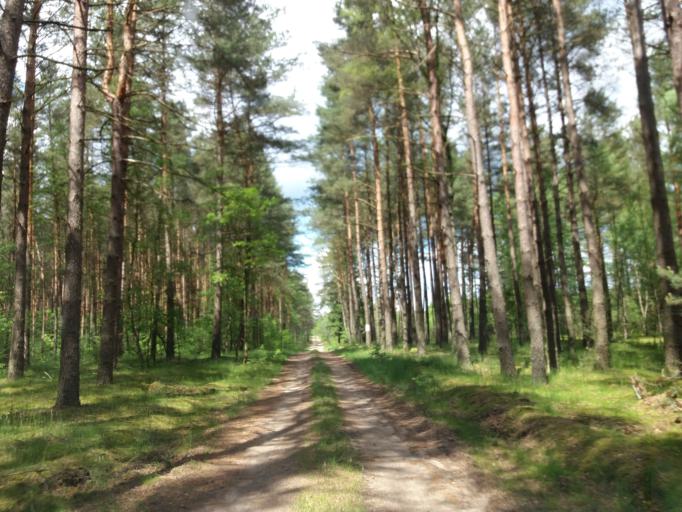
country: PL
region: West Pomeranian Voivodeship
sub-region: Powiat choszczenski
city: Drawno
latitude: 53.2506
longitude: 15.7519
